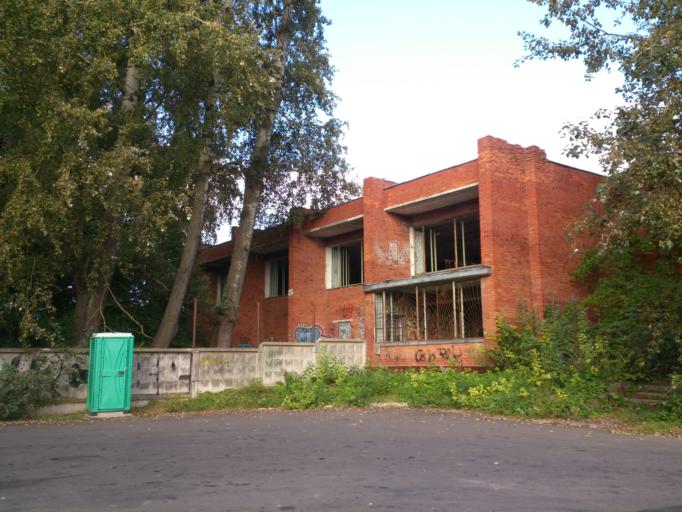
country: LT
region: Kauno apskritis
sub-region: Kaunas
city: Aleksotas
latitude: 54.8751
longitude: 23.9141
